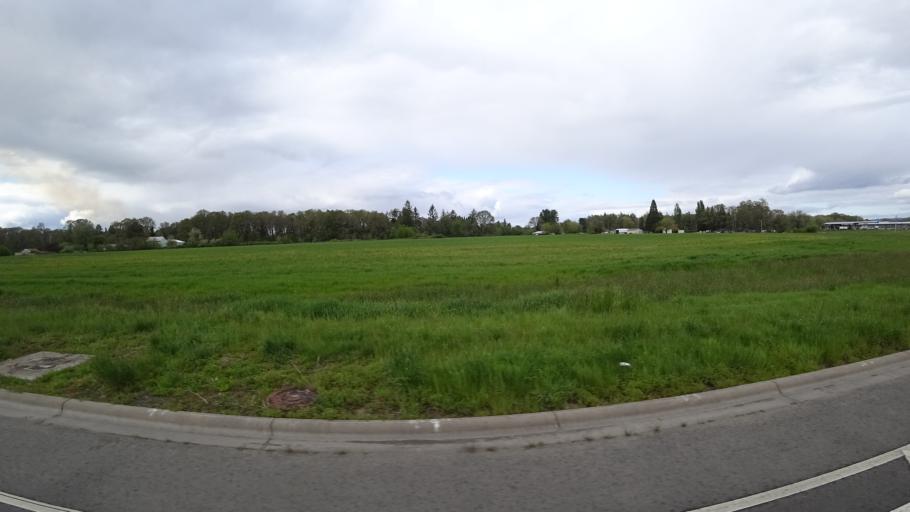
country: US
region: Oregon
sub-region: Washington County
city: Hillsboro
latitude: 45.5516
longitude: -122.9566
